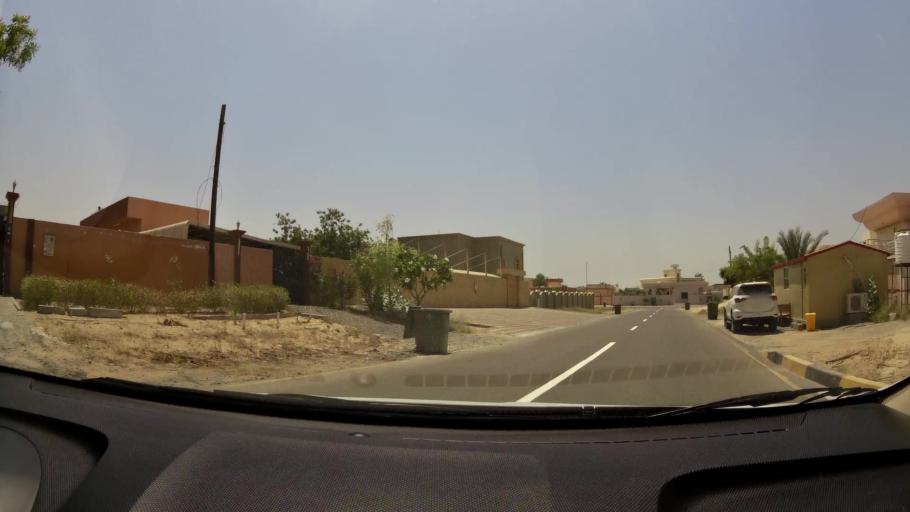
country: AE
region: Ajman
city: Ajman
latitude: 25.4260
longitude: 55.5143
